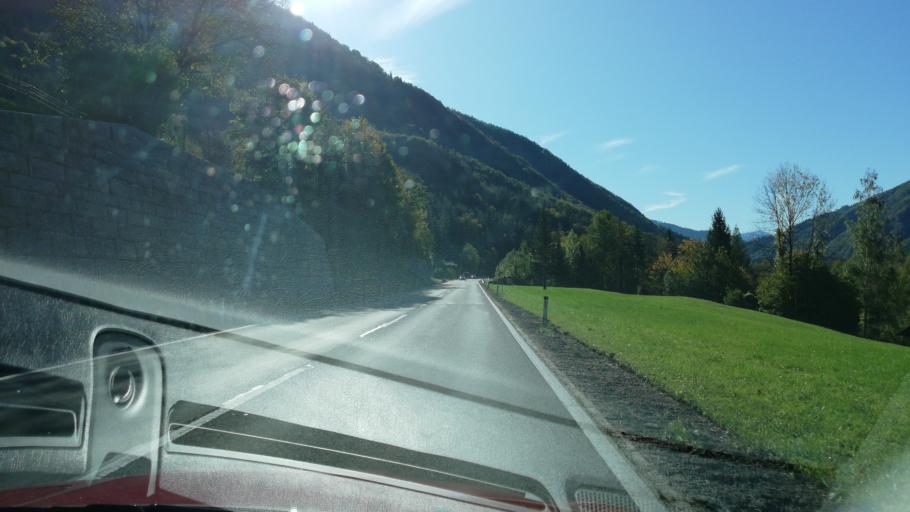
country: AT
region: Upper Austria
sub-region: Politischer Bezirk Steyr-Land
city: Weyer
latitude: 47.8087
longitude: 14.6448
